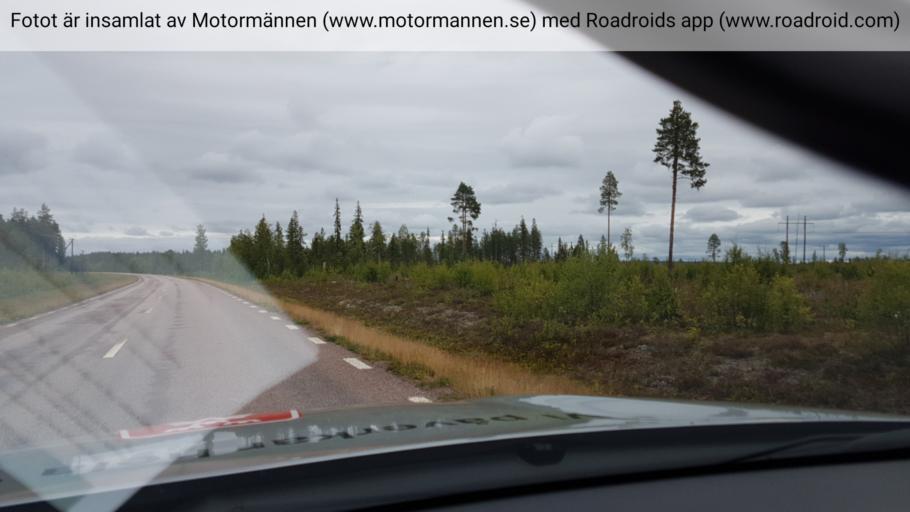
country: SE
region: Norrbotten
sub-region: Pajala Kommun
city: Pajala
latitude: 67.1038
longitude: 22.5934
